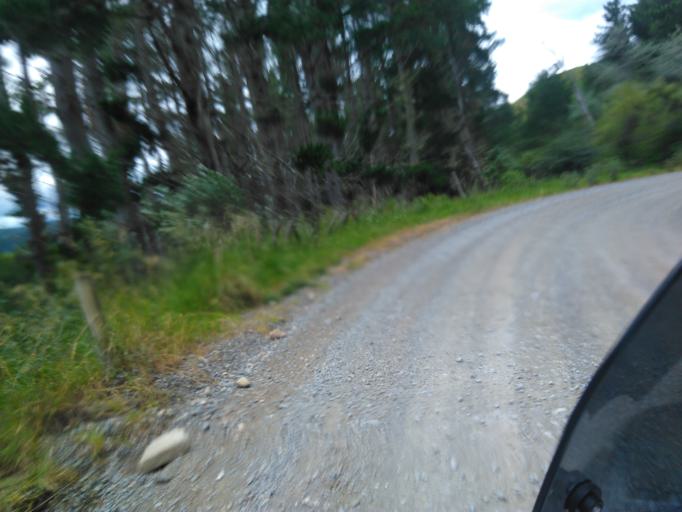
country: NZ
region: Gisborne
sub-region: Gisborne District
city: Gisborne
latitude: -38.0531
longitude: 178.1037
